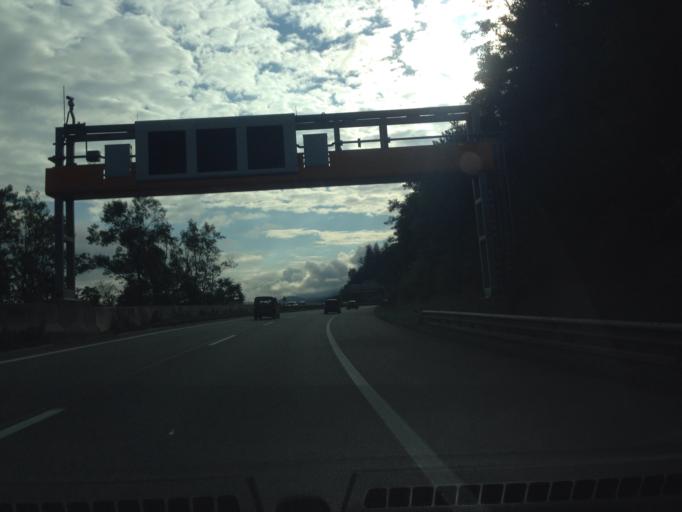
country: AT
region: Tyrol
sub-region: Innsbruck Stadt
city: Innsbruck
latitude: 47.2535
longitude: 11.3785
